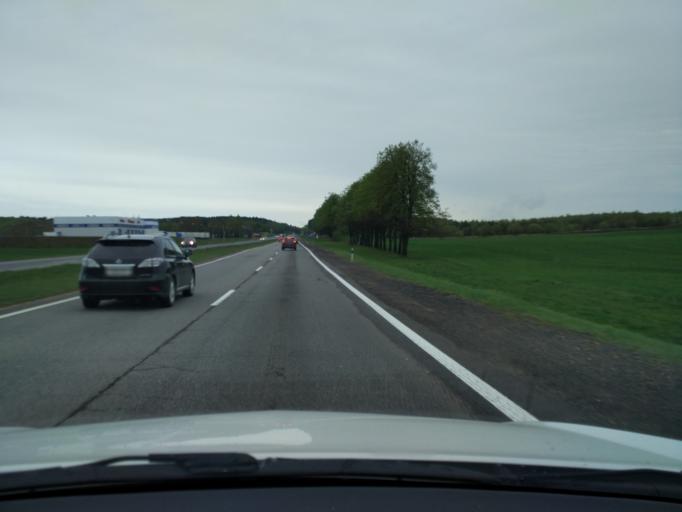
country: BY
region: Minsk
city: Luhavaya Slabada
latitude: 53.7544
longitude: 27.8317
